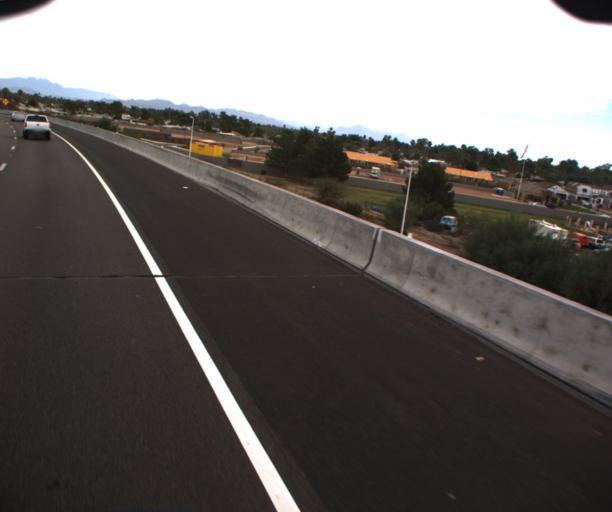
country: US
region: Arizona
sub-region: Maricopa County
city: Mesa
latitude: 33.4453
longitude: -111.8561
